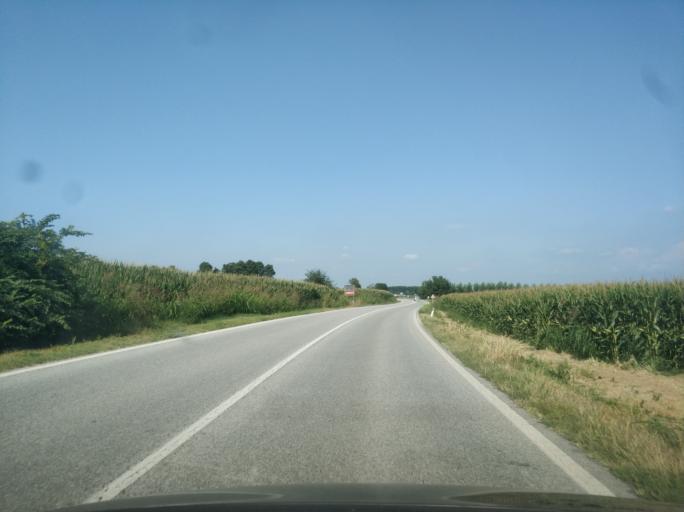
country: IT
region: Piedmont
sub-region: Provincia di Cuneo
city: Centallo
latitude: 44.5196
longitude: 7.5994
